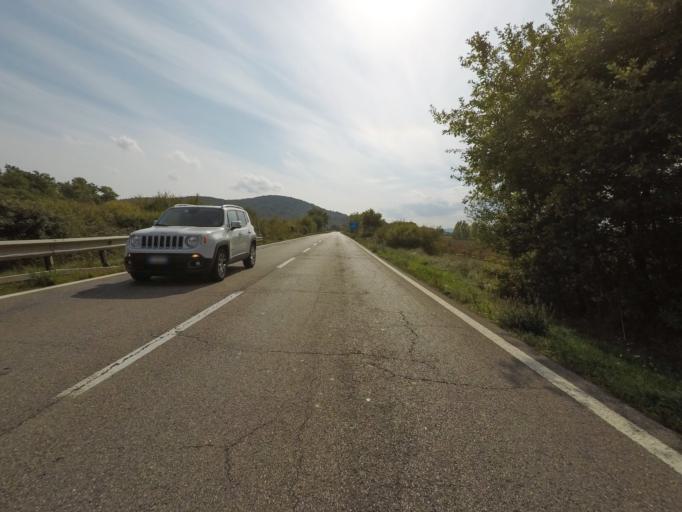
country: IT
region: Tuscany
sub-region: Provincia di Siena
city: Rosia
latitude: 43.2128
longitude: 11.2777
